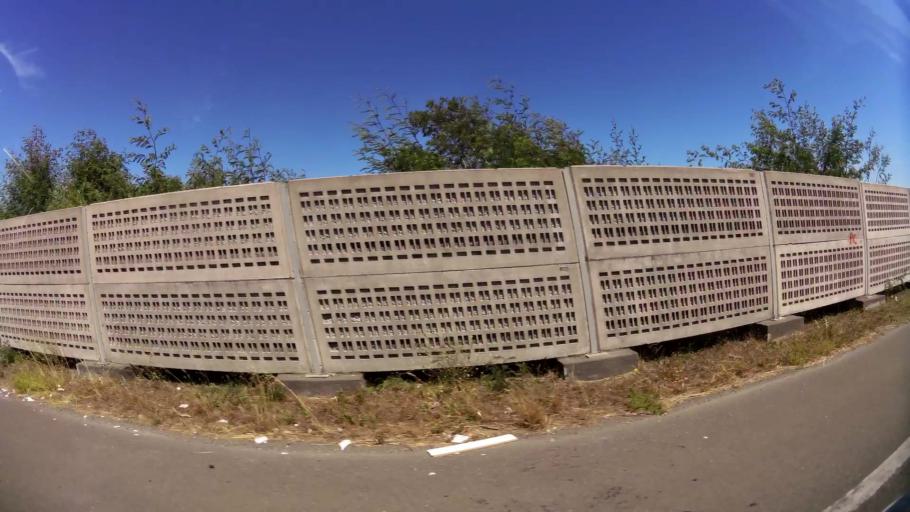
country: CL
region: Biobio
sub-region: Provincia de Concepcion
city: Talcahuano
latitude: -36.7314
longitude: -73.0978
